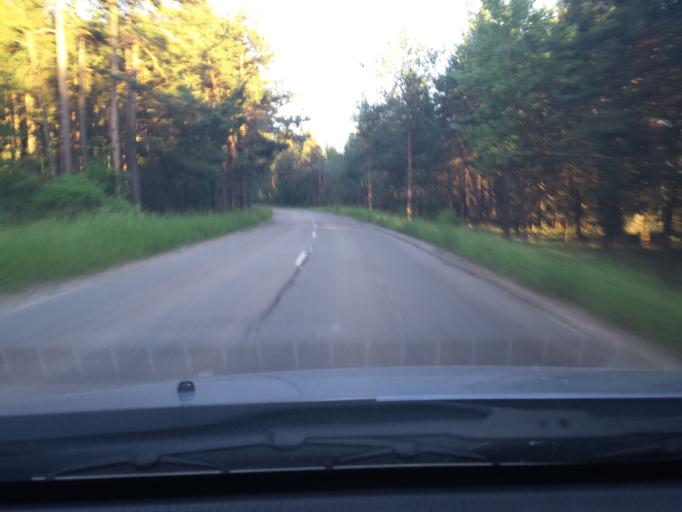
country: LV
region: Riga
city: Jaunciems
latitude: 57.0283
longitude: 24.1898
